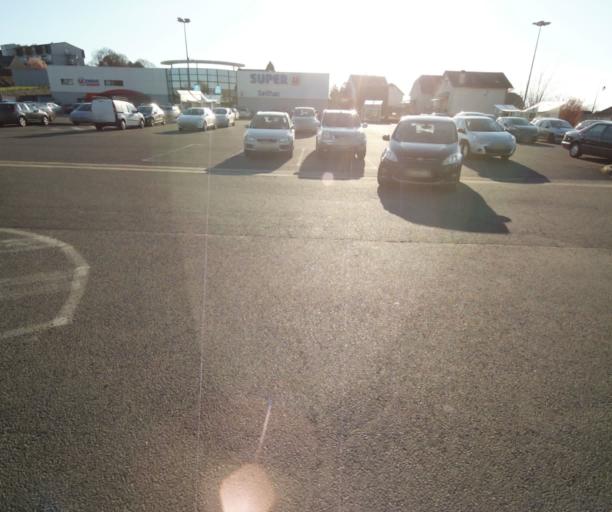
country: FR
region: Limousin
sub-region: Departement de la Correze
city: Seilhac
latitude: 45.3683
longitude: 1.7186
